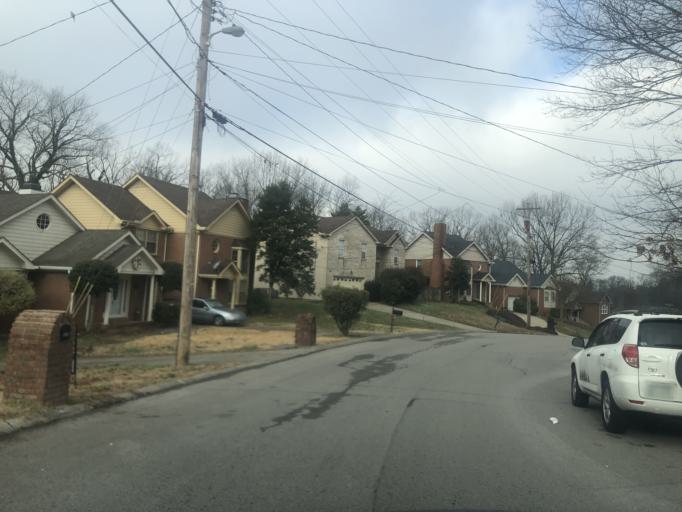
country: US
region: Tennessee
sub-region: Rutherford County
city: La Vergne
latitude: 36.0715
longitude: -86.6621
